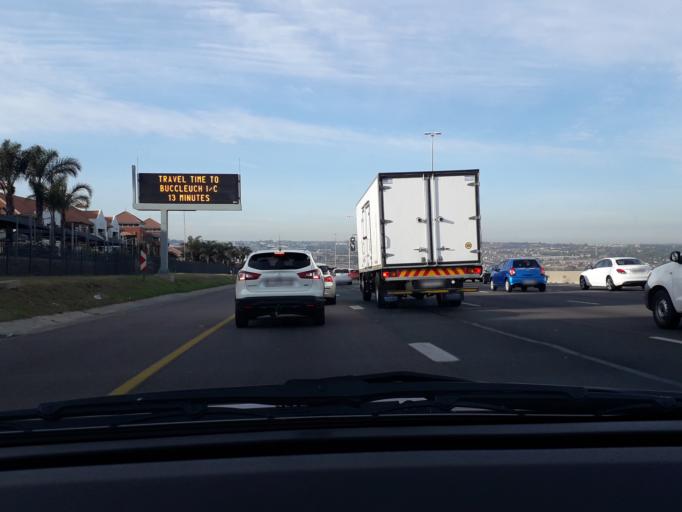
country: ZA
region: Gauteng
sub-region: City of Johannesburg Metropolitan Municipality
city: Midrand
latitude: -25.9427
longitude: 28.1386
